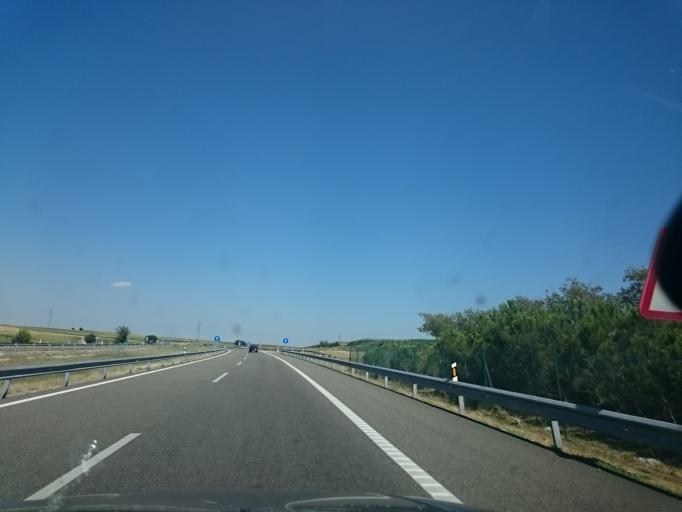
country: ES
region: Aragon
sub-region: Provincia de Huesca
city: Valfarta
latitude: 41.5176
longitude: -0.0973
